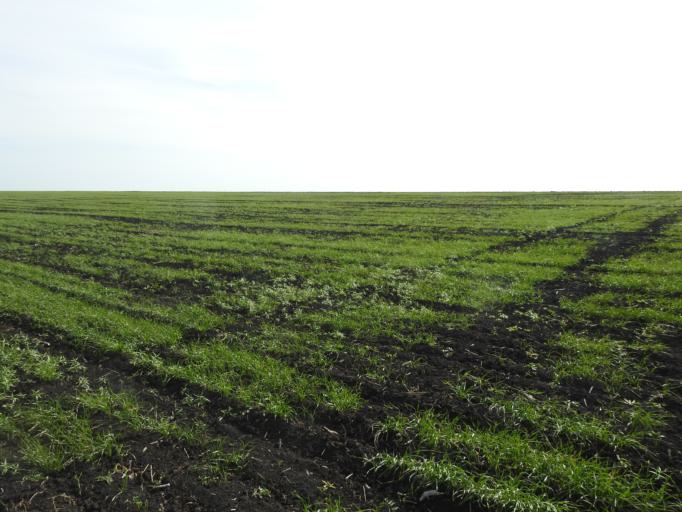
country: RU
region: Saratov
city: Baltay
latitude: 52.5461
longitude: 46.7140
